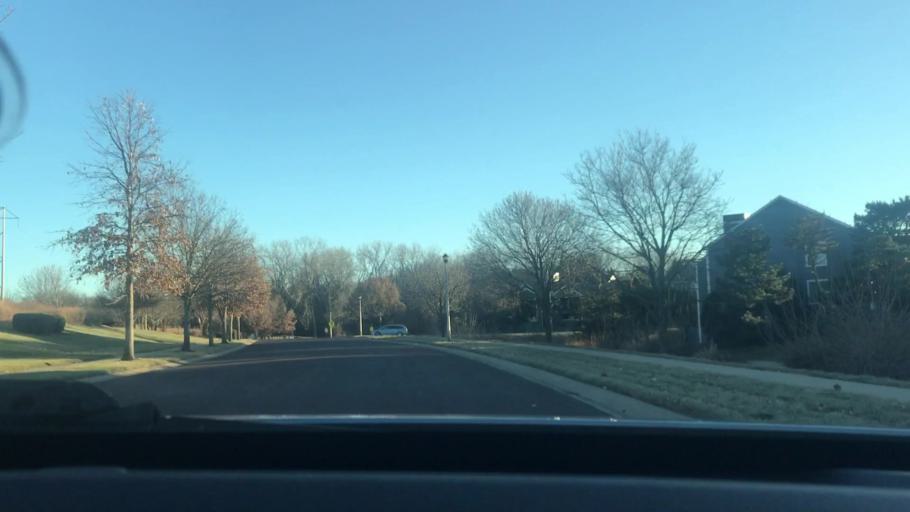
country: US
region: Kansas
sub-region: Johnson County
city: Overland Park
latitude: 38.9834
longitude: -94.7009
